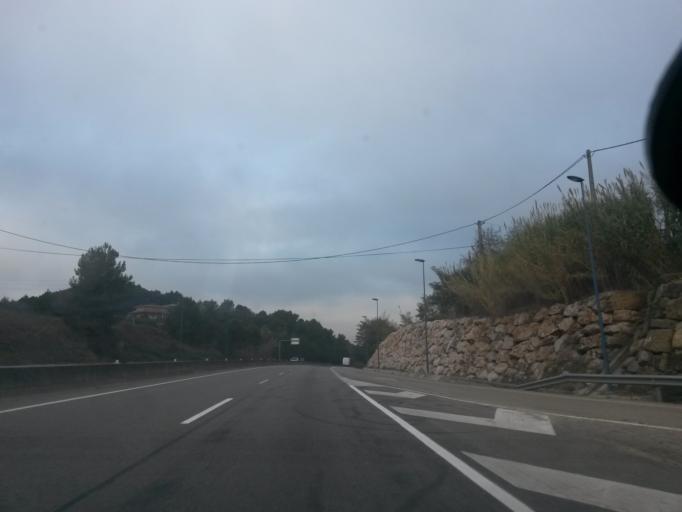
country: ES
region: Catalonia
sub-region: Provincia de Girona
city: Palol de Revardit
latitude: 42.0586
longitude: 2.8142
